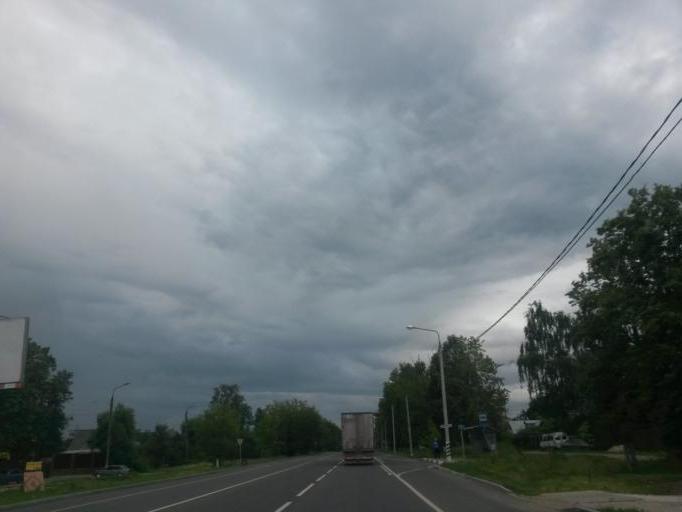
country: RU
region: Moskovskaya
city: L'vovskiy
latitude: 55.3232
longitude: 37.5285
